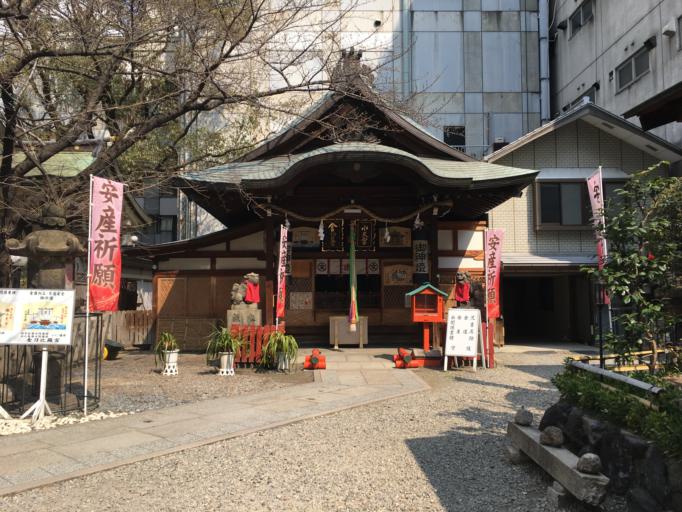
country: JP
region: Osaka
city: Osaka-shi
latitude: 34.6992
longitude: 135.5010
